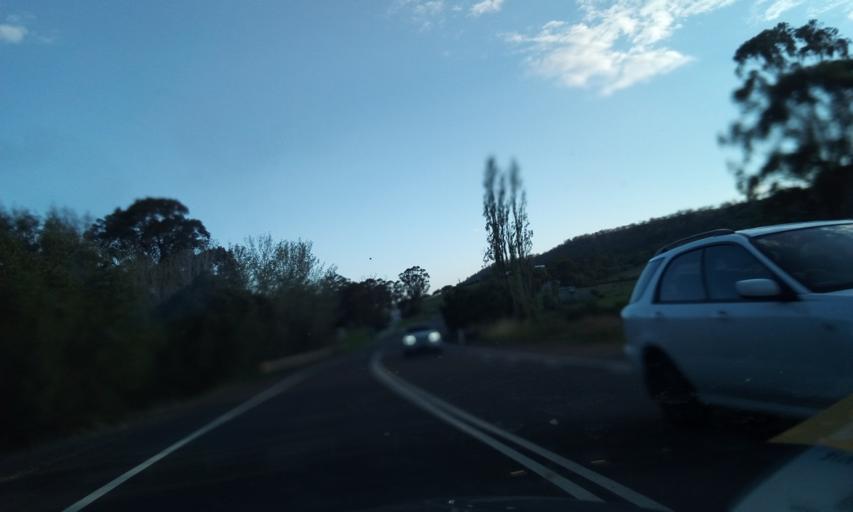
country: AU
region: New South Wales
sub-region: Camden
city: Camden South
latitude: -34.1191
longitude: 150.6995
